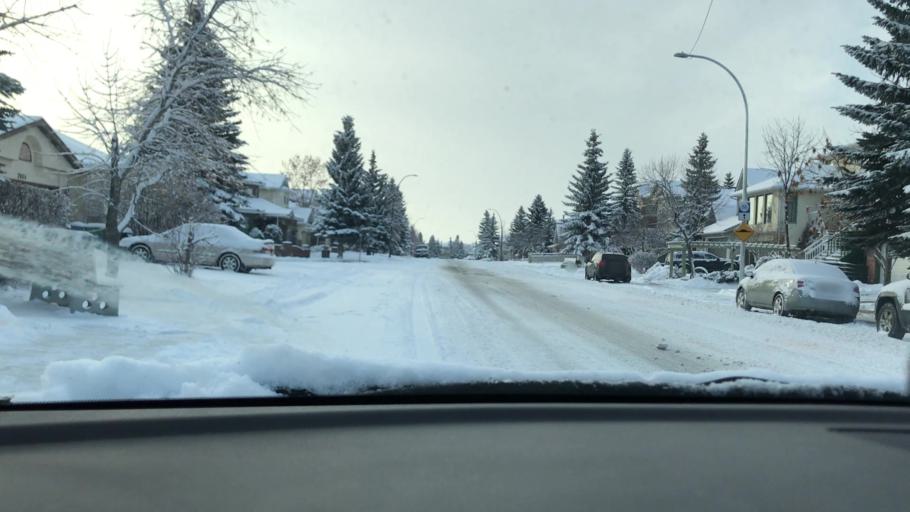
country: CA
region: Alberta
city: Calgary
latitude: 51.0274
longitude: -114.1701
